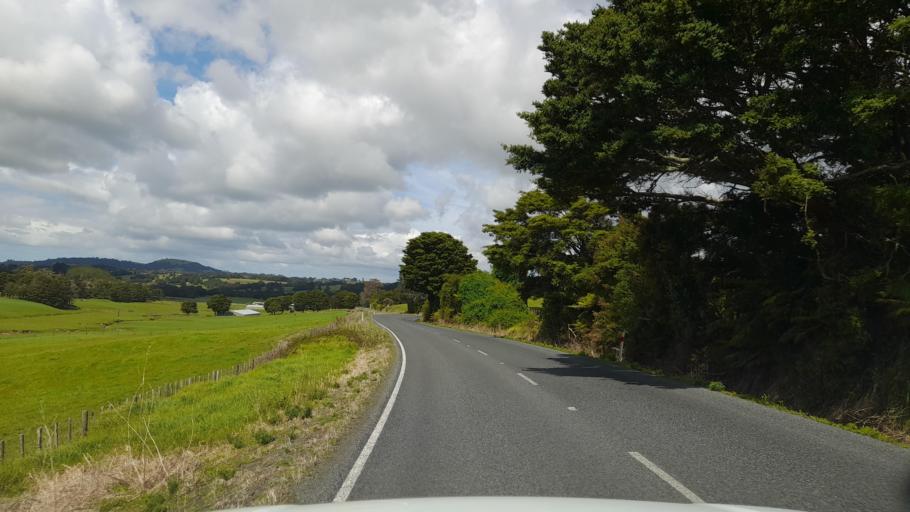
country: NZ
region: Northland
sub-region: Whangarei
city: Maungatapere
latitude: -35.6533
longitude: 174.1266
